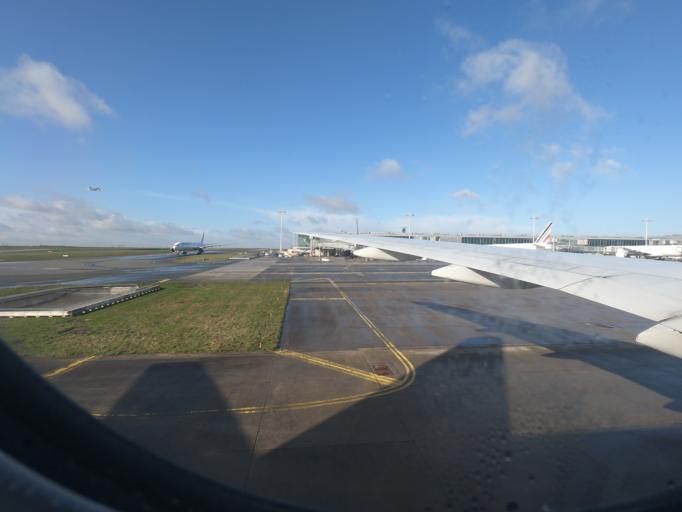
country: FR
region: Ile-de-France
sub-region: Departement de Seine-et-Marne
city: Mitry-Mory
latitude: 49.0012
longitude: 2.5889
